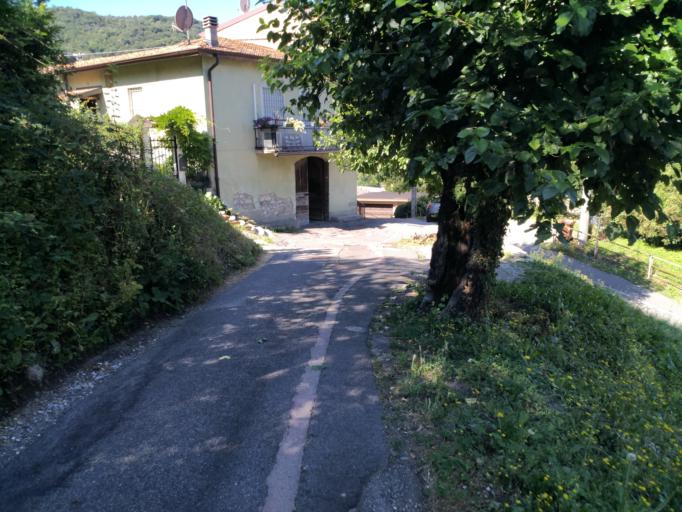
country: CH
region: Ticino
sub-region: Mendrisio District
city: Chiasso
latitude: 45.8315
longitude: 9.0405
